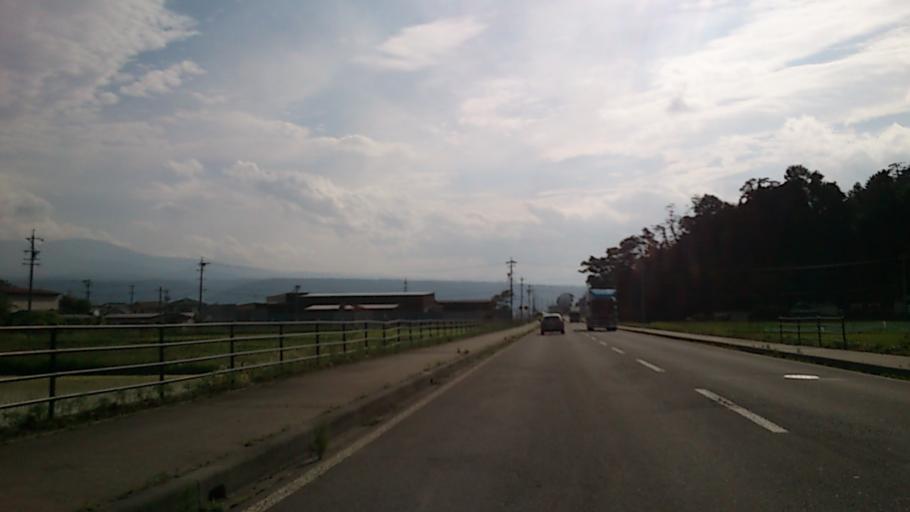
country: JP
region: Nagano
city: Saku
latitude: 36.2341
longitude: 138.5088
